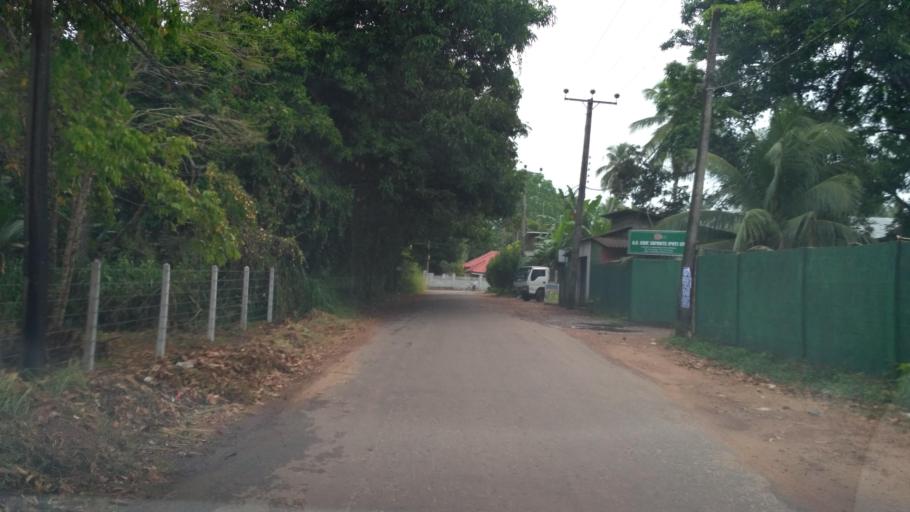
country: LK
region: North Western
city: Kuliyapitiya
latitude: 7.3262
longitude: 80.0228
